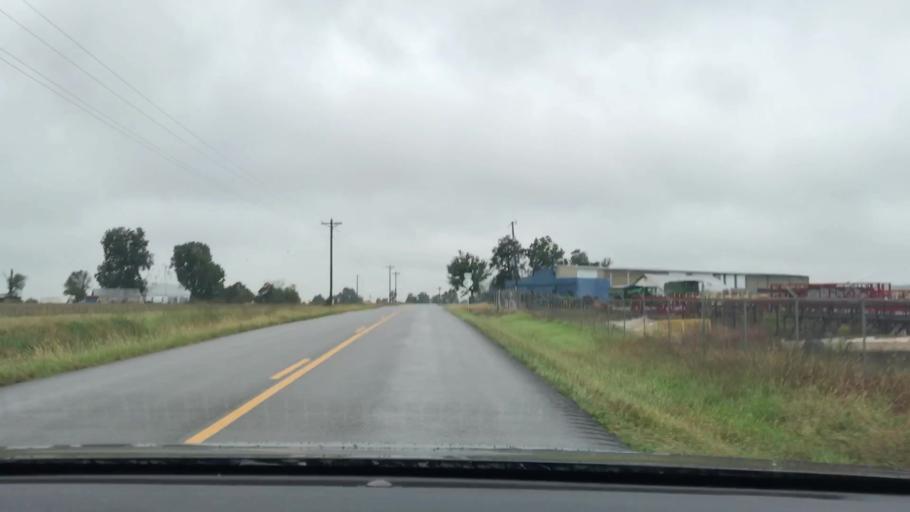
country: US
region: Kentucky
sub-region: Hopkins County
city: Madisonville
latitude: 37.3731
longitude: -87.3519
